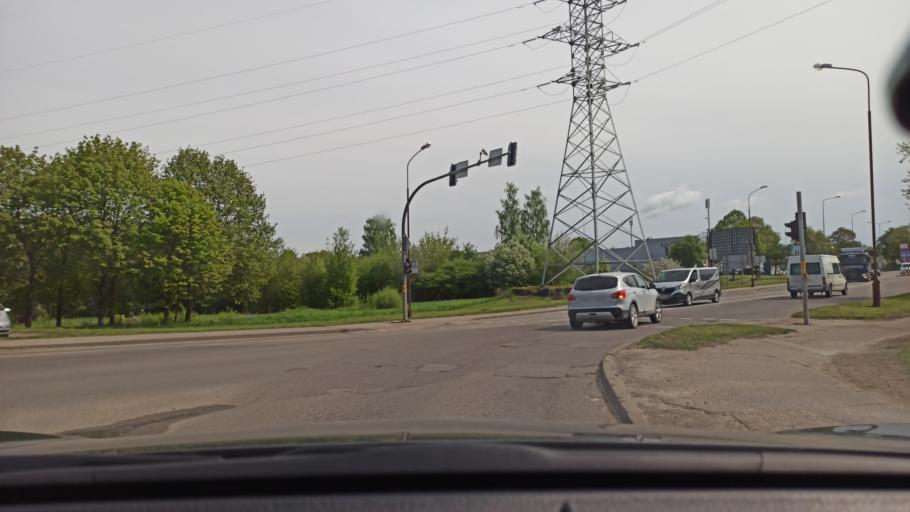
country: LT
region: Siauliu apskritis
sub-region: Siauliai
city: Siauliai
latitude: 55.9230
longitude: 23.3510
